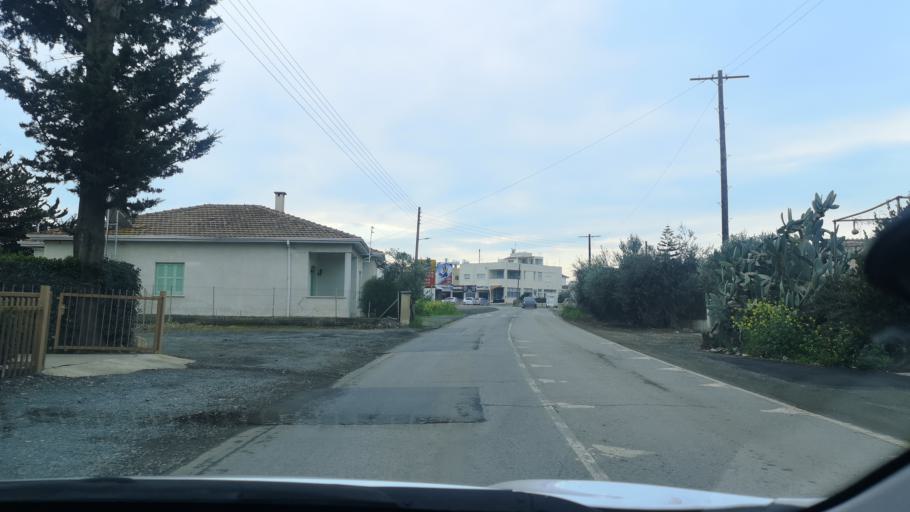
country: CY
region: Lefkosia
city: Kato Deftera
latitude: 35.0843
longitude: 33.2755
